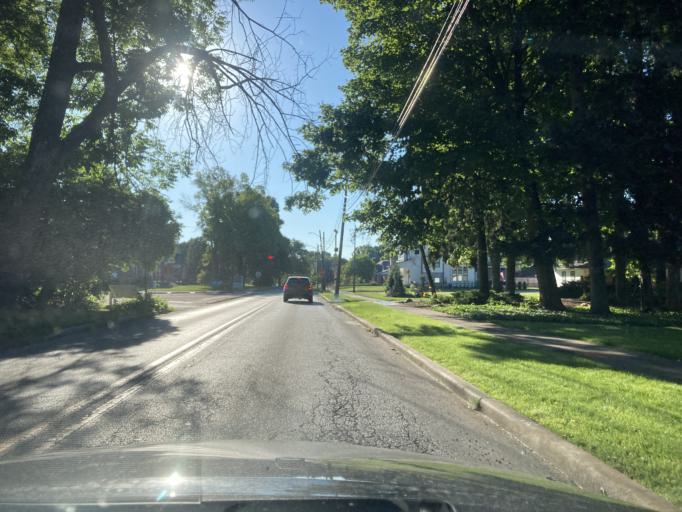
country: US
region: Indiana
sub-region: Marion County
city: Broad Ripple
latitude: 39.8394
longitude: -86.1627
